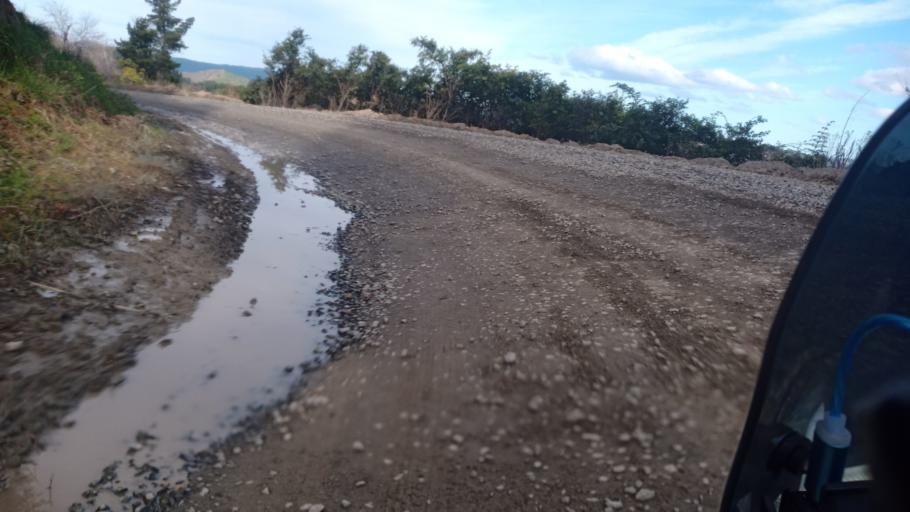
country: NZ
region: Gisborne
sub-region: Gisborne District
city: Gisborne
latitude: -38.1289
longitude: 178.1767
